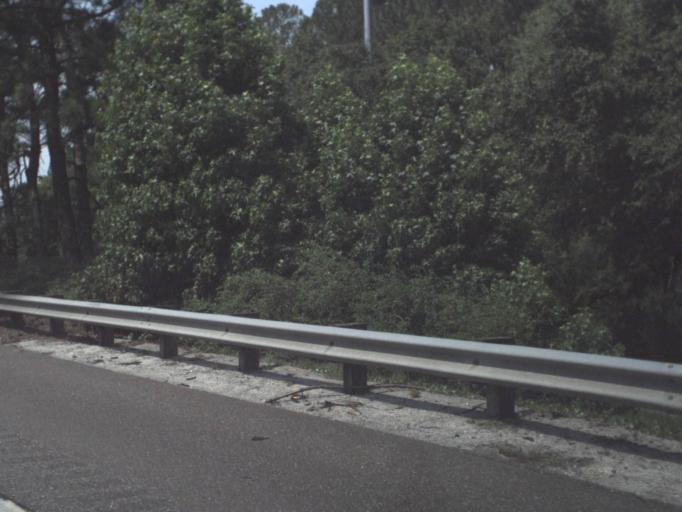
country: US
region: Florida
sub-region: Duval County
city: Jacksonville
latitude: 30.4837
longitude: -81.6434
